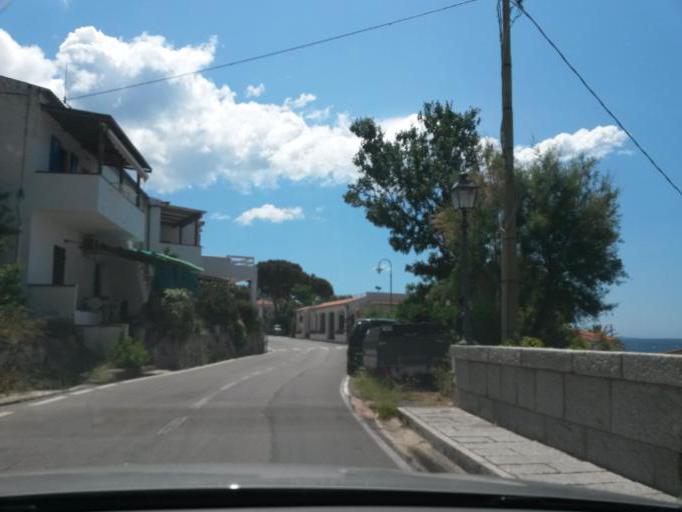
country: IT
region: Tuscany
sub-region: Provincia di Livorno
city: Marciana
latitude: 42.7602
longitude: 10.1124
